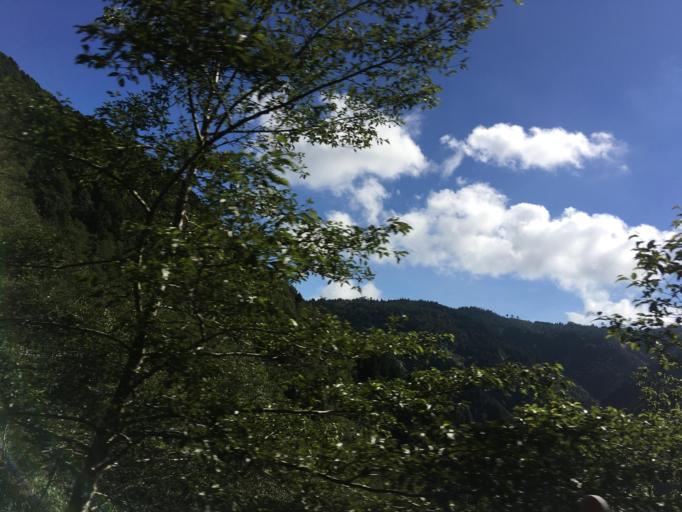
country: TW
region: Taiwan
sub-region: Yilan
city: Yilan
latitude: 24.5111
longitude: 121.5683
